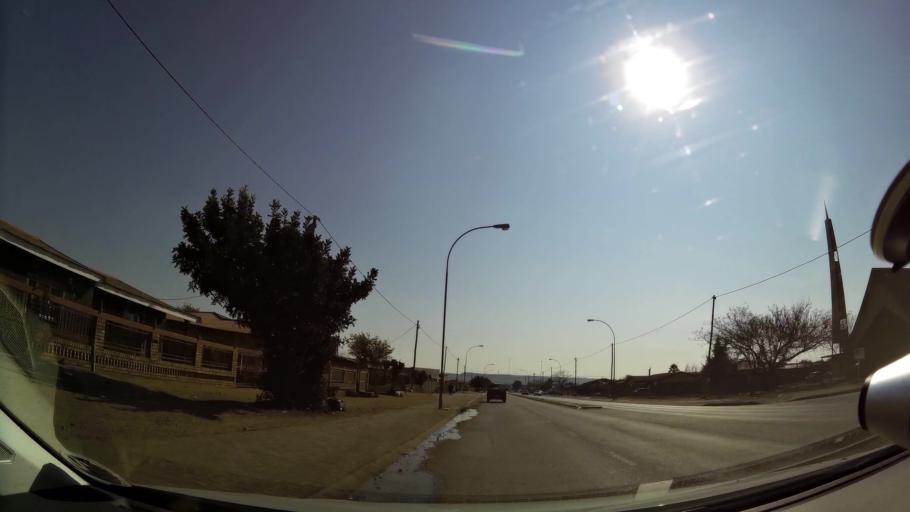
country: ZA
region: Orange Free State
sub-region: Mangaung Metropolitan Municipality
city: Bloemfontein
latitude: -29.1519
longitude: 26.2405
